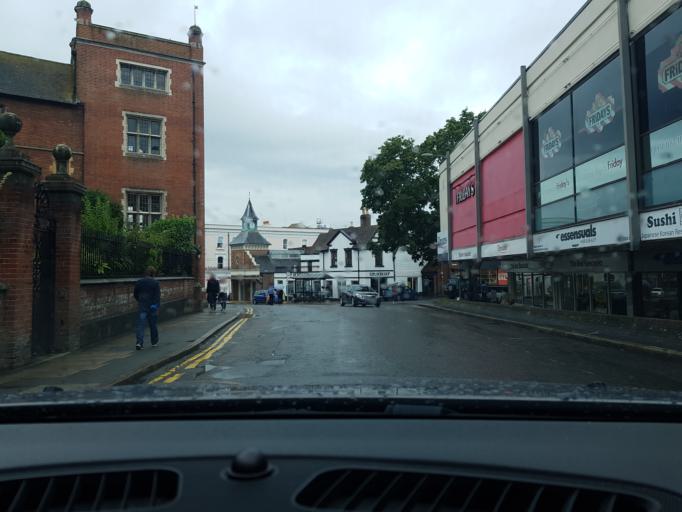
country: GB
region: England
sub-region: Surrey
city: Guildford
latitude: 51.2369
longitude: -0.5710
